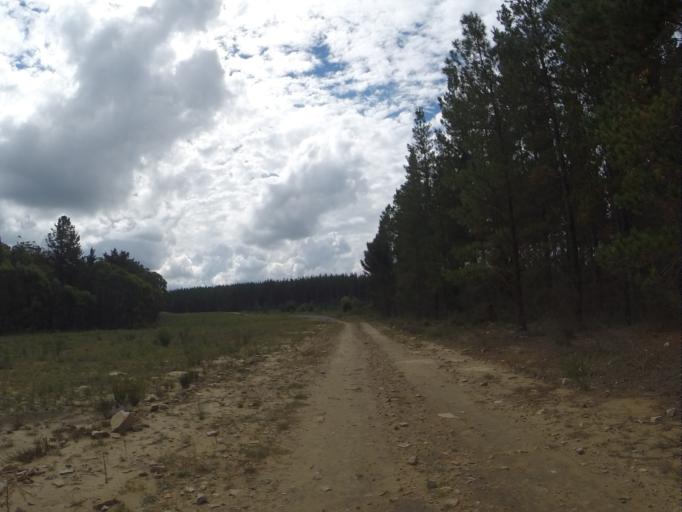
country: AU
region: New South Wales
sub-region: Wingecarribee
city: Moss Vale
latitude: -34.5187
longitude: 150.2271
